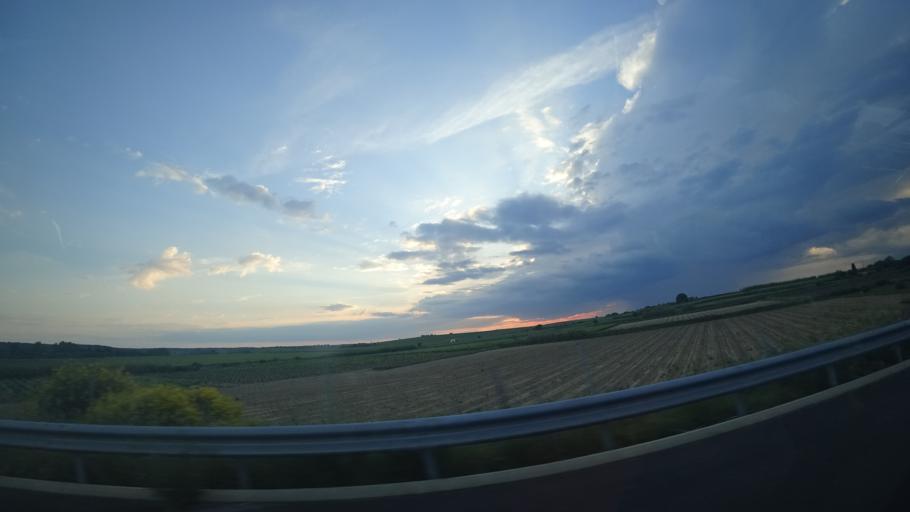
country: FR
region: Languedoc-Roussillon
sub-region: Departement de l'Herault
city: Paulhan
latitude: 43.5188
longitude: 3.4433
